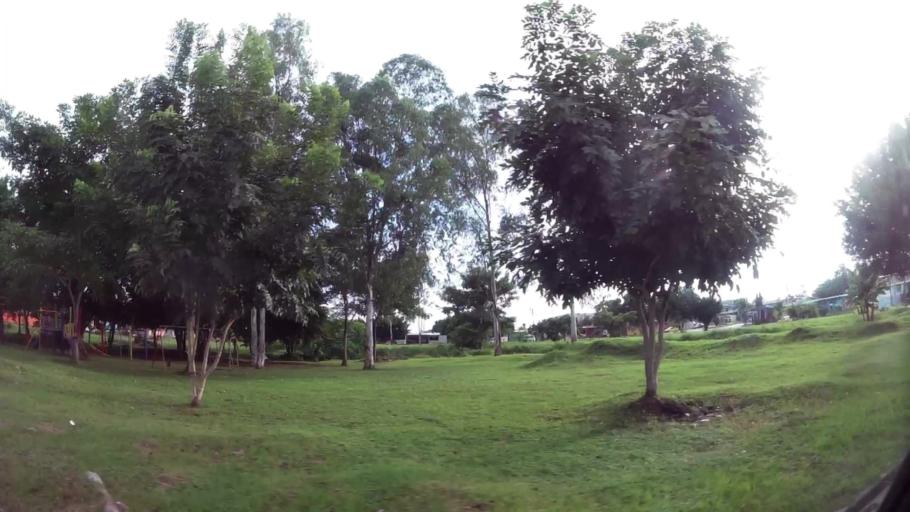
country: PA
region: Panama
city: Tocumen
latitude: 9.0785
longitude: -79.3621
